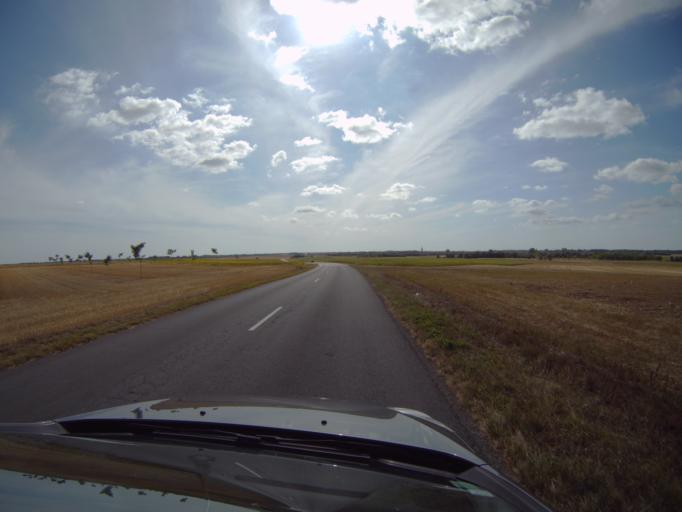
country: FR
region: Poitou-Charentes
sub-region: Departement des Deux-Sevres
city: Saint-Hilaire-la-Palud
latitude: 46.2640
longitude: -0.6884
